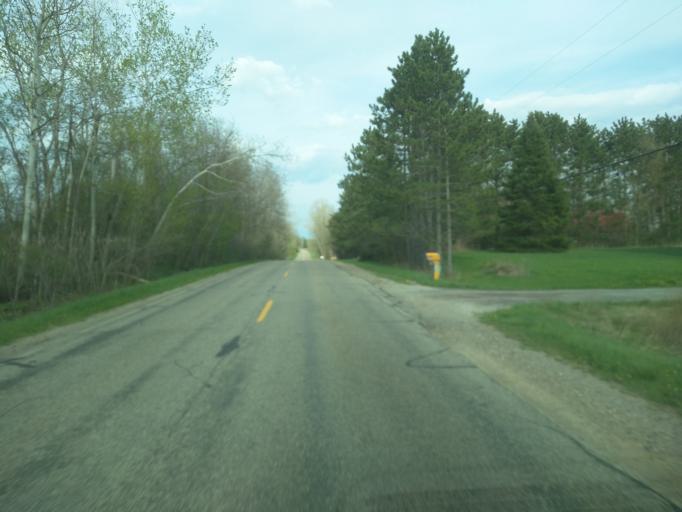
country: US
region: Michigan
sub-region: Eaton County
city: Dimondale
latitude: 42.6257
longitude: -84.6348
